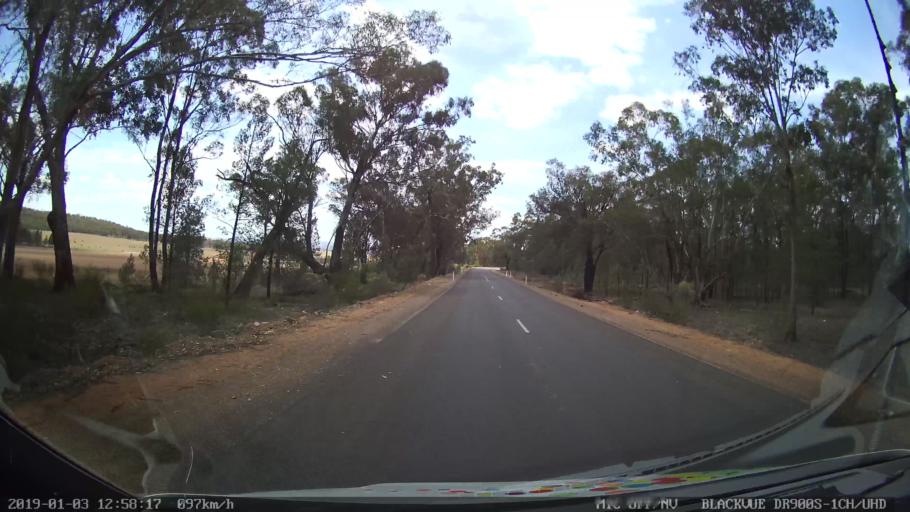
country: AU
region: New South Wales
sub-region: Cabonne
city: Canowindra
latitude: -33.6433
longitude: 148.3731
